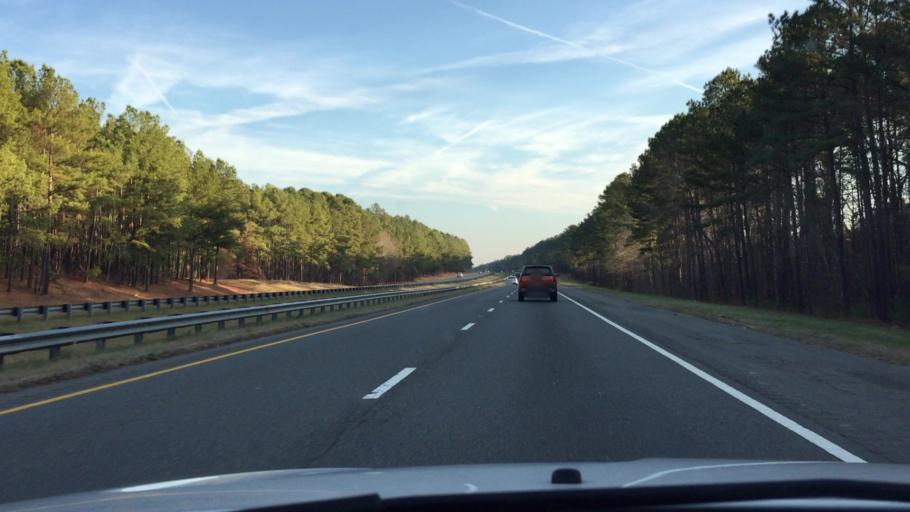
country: US
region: North Carolina
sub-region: Chatham County
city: Farmville
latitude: 35.5426
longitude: -79.1696
